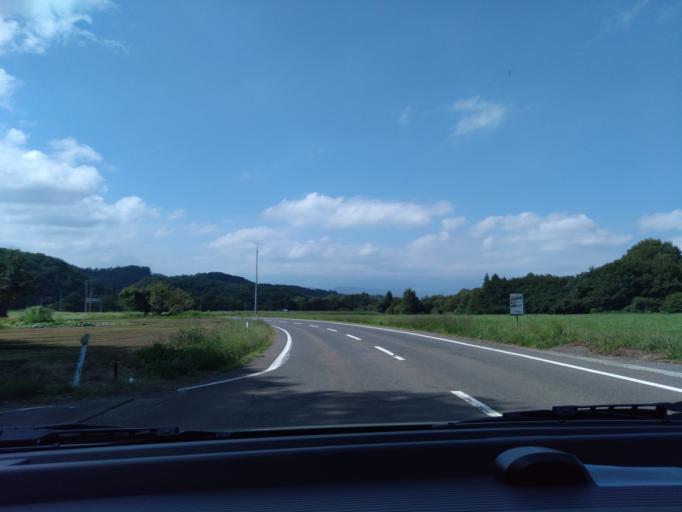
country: JP
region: Iwate
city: Shizukuishi
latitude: 39.6432
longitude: 141.0020
